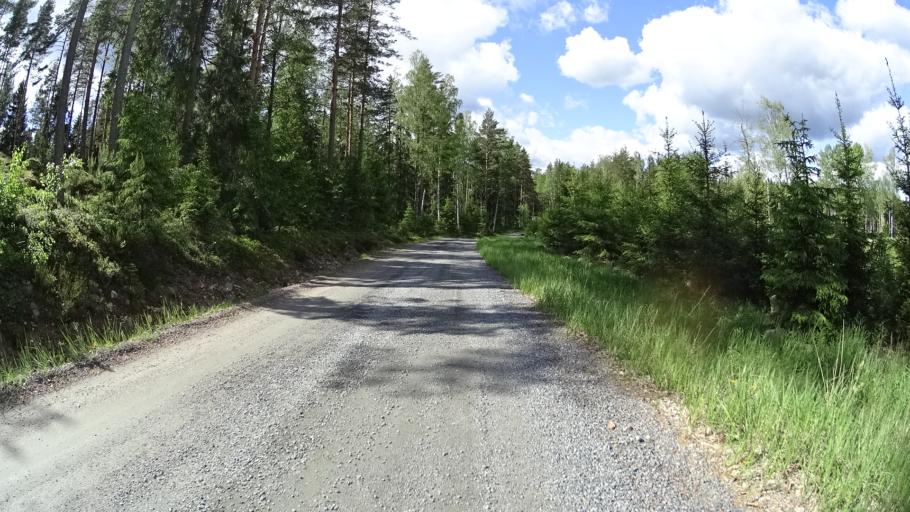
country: FI
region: Uusimaa
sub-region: Raaseporin
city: Pohja
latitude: 60.1800
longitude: 23.5872
